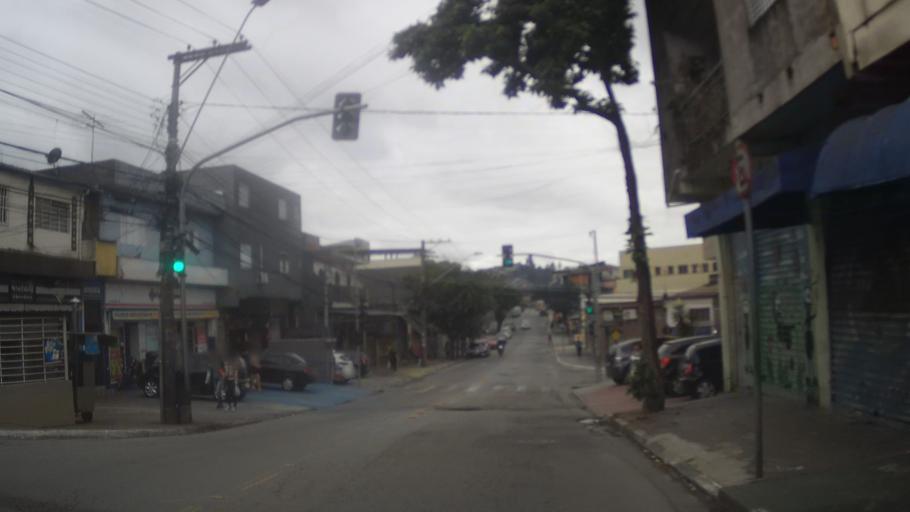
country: BR
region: Sao Paulo
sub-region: Guarulhos
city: Guarulhos
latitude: -23.4260
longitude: -46.5340
